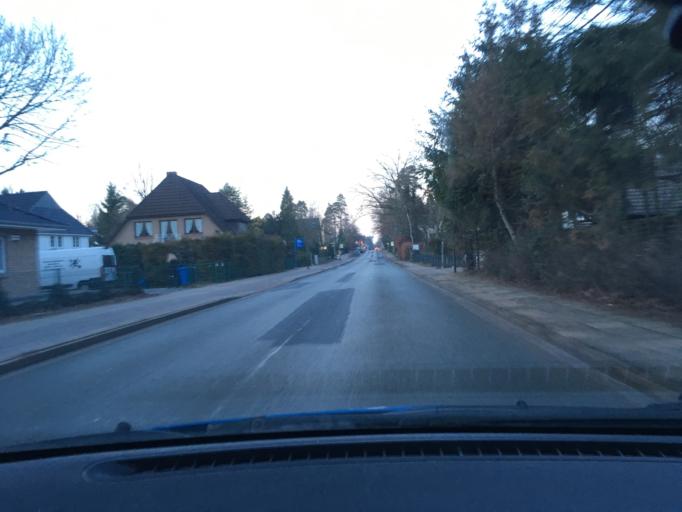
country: DE
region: Lower Saxony
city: Buchholz in der Nordheide
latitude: 53.2816
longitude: 9.8719
